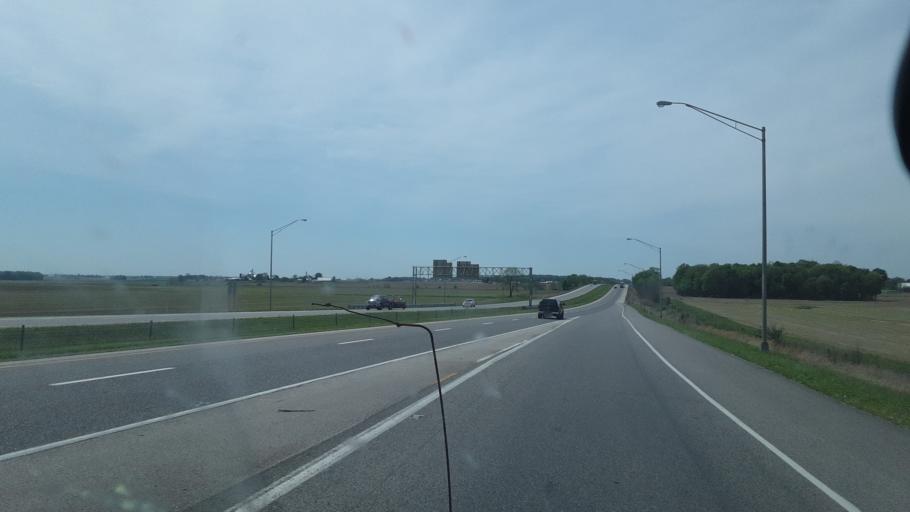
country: US
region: Indiana
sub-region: Gibson County
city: Haubstadt
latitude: 38.1673
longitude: -87.5551
